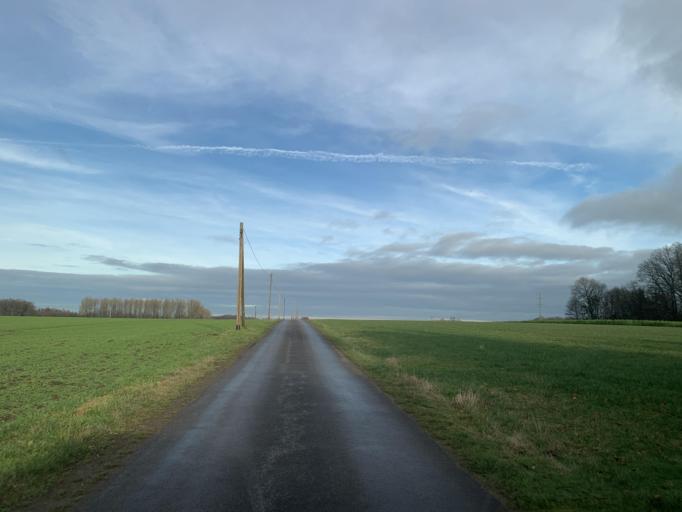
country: DE
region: North Rhine-Westphalia
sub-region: Regierungsbezirk Munster
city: Dulmen
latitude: 51.7931
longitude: 7.3590
